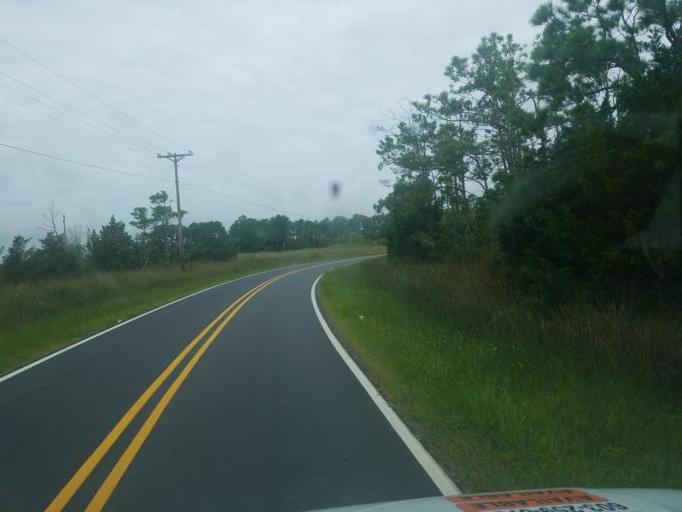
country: US
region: North Carolina
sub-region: Dare County
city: Manteo
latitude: 35.8761
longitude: -75.7566
